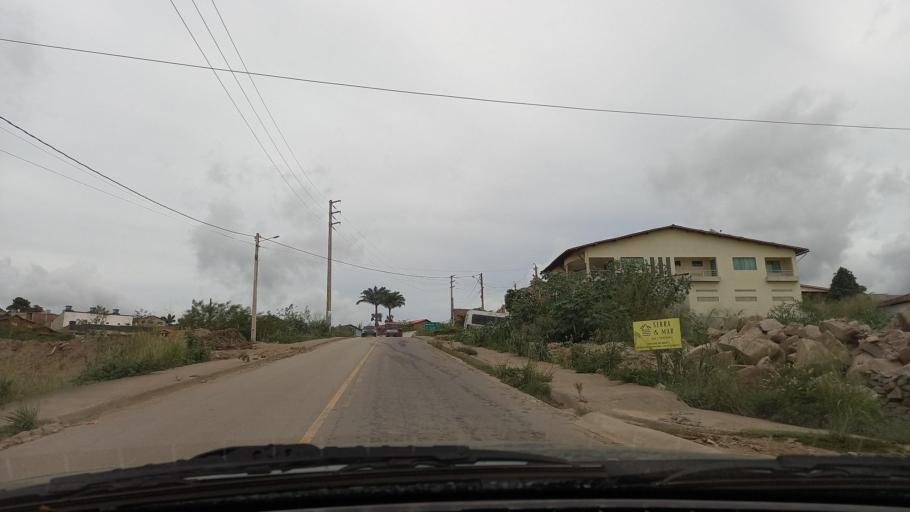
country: BR
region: Pernambuco
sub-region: Gravata
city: Gravata
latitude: -8.2119
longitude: -35.5787
